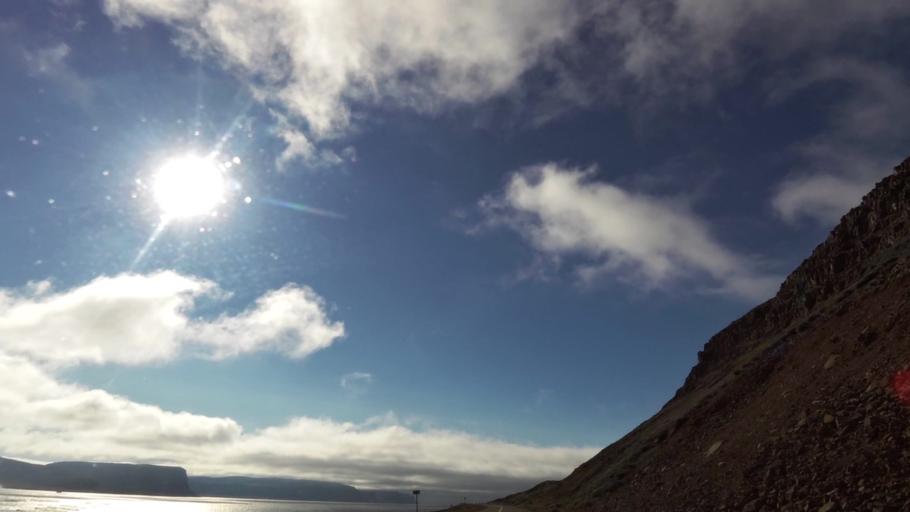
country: IS
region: West
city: Olafsvik
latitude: 65.5804
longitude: -23.9540
